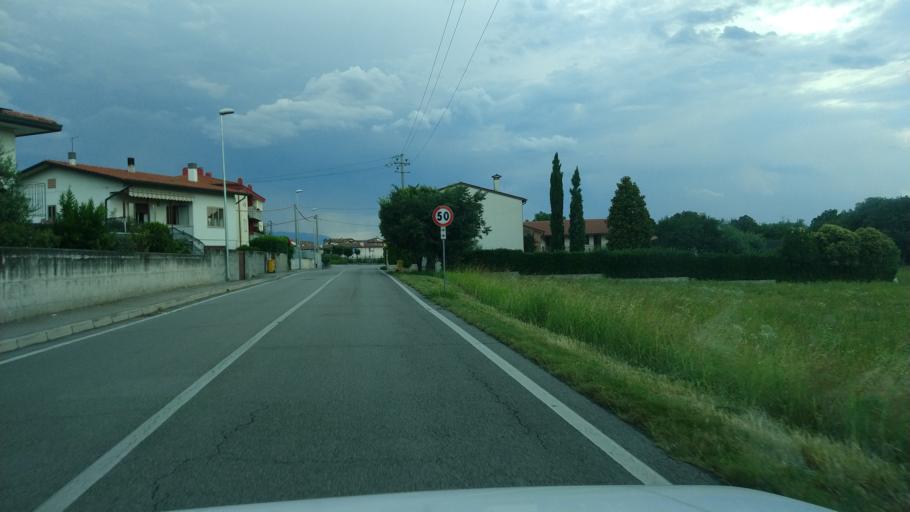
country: IT
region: Veneto
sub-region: Provincia di Vicenza
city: Bassano del Grappa
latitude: 45.7562
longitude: 11.7084
